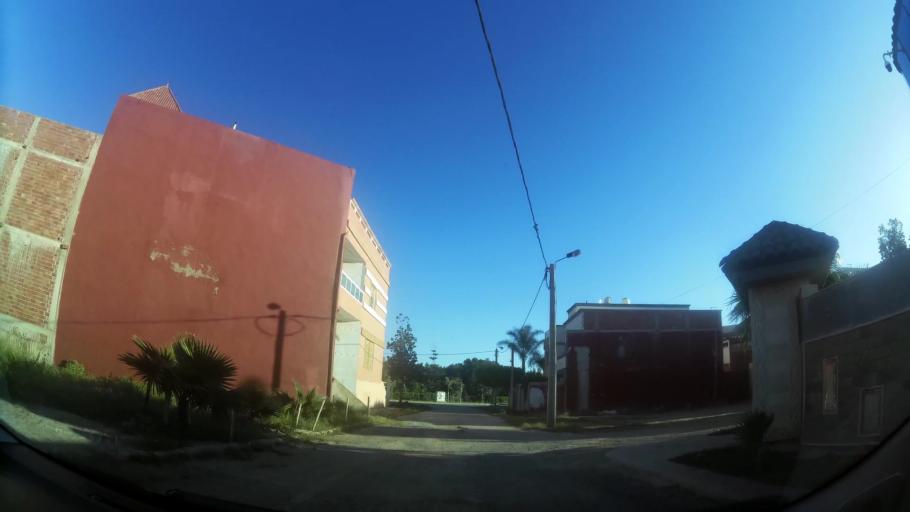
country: MA
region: Oriental
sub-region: Berkane-Taourirt
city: Madagh
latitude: 35.0874
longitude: -2.2463
